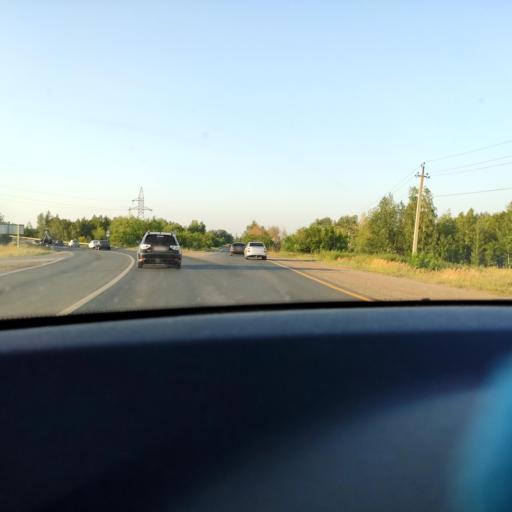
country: RU
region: Samara
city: Kinel'
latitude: 53.2479
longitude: 50.5900
